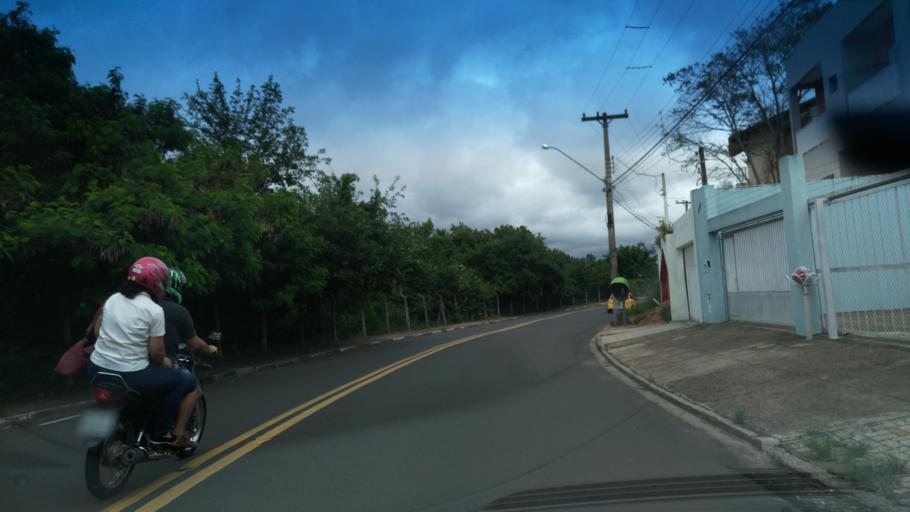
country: BR
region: Sao Paulo
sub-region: Valinhos
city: Valinhos
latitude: -22.9600
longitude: -46.9774
